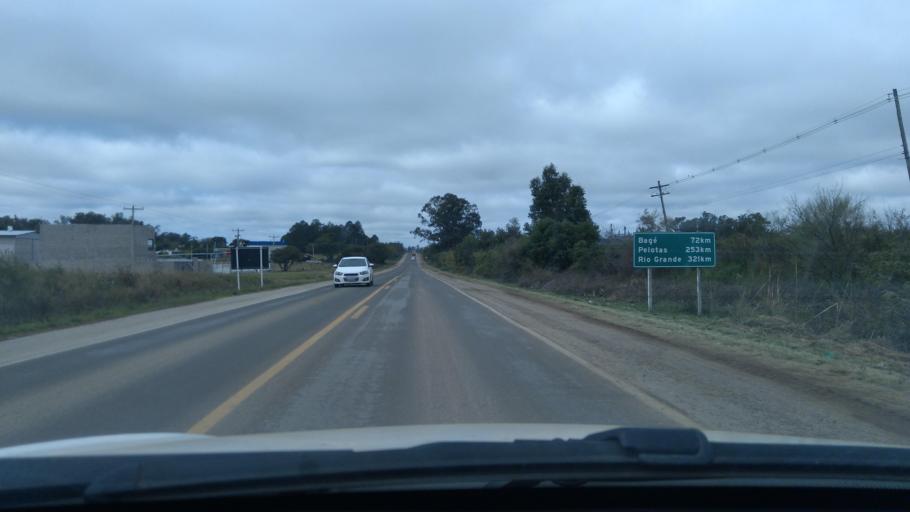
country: BR
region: Rio Grande do Sul
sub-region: Dom Pedrito
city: Dom Pedrito
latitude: -30.9688
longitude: -54.6608
